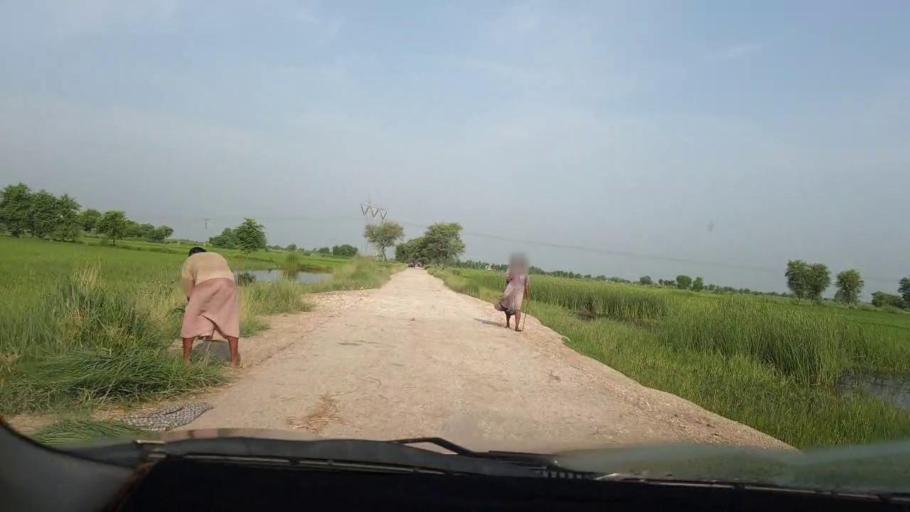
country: PK
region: Sindh
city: Goth Garelo
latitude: 27.4818
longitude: 68.0830
